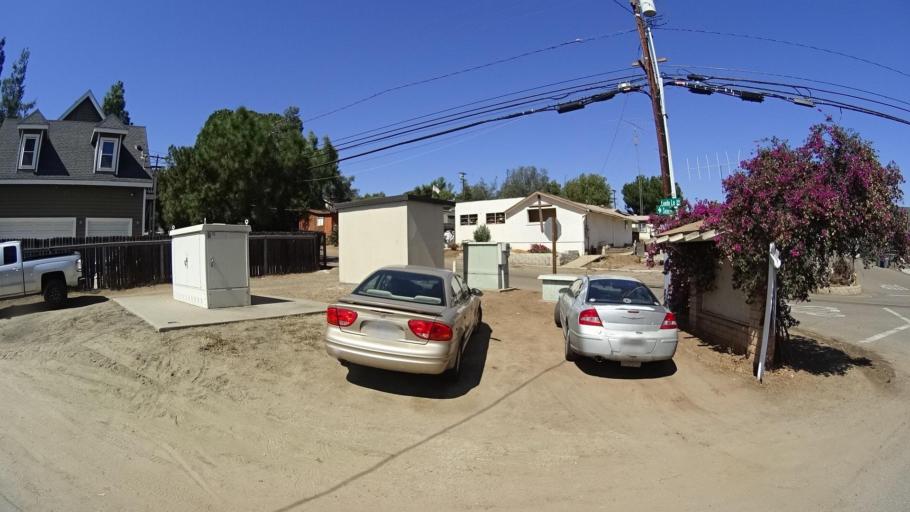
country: US
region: California
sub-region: San Diego County
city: Crest
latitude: 32.8057
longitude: -116.8662
